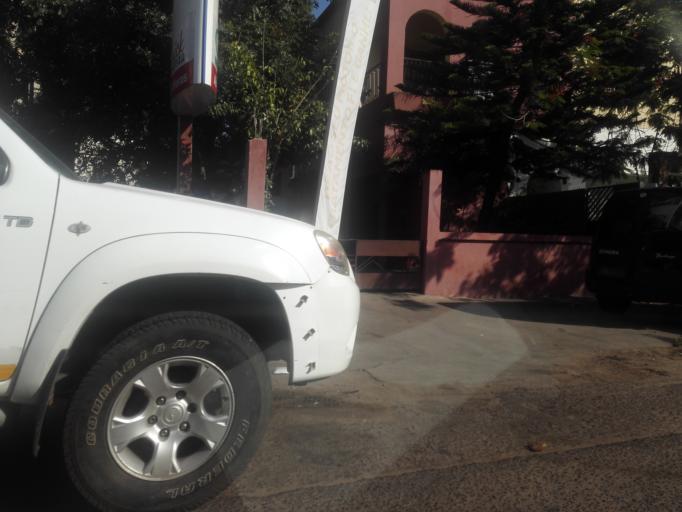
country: MZ
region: Maputo City
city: Maputo
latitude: -25.9593
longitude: 32.5841
